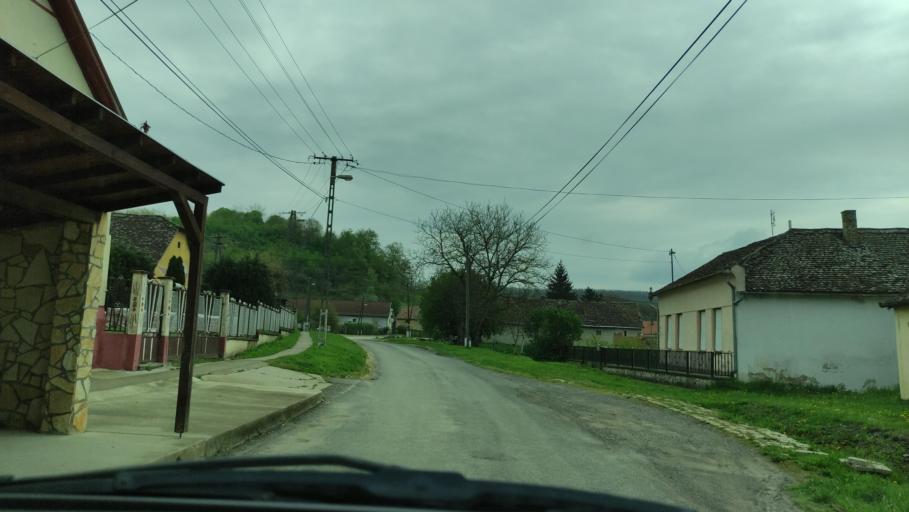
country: HU
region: Baranya
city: Magocs
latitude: 46.2956
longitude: 18.2037
